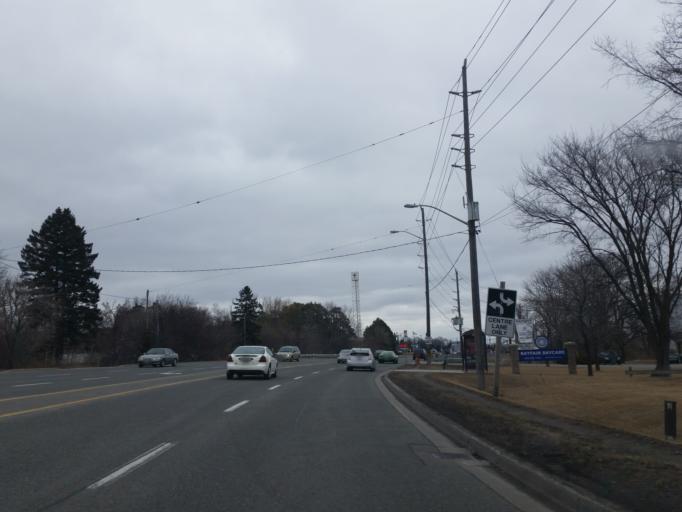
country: CA
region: Ontario
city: Pickering
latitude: 43.8222
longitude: -79.1109
